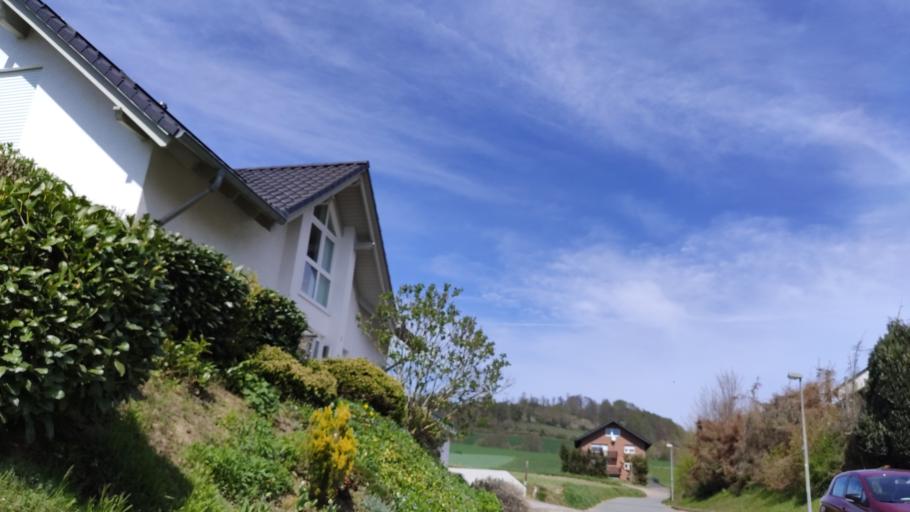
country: DE
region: North Rhine-Westphalia
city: Beverungen
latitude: 51.7126
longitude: 9.3060
